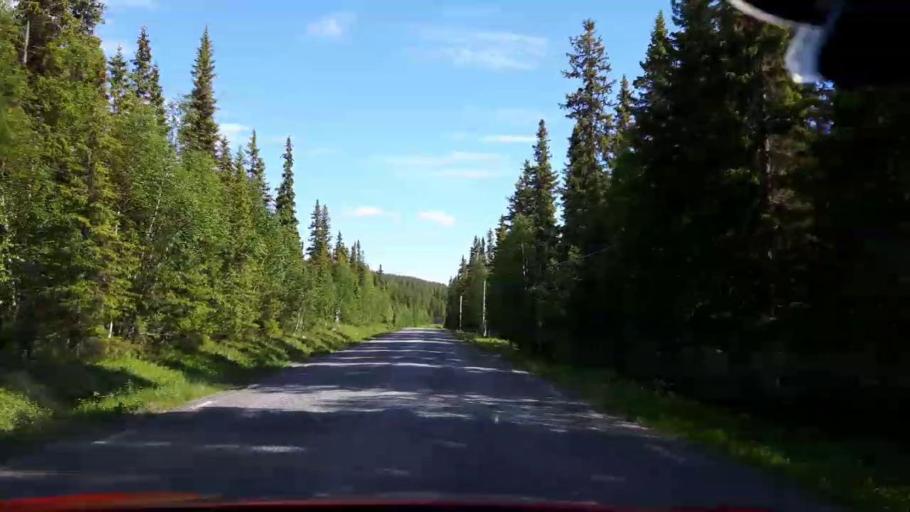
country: SE
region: Jaemtland
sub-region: Krokoms Kommun
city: Valla
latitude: 63.7541
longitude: 14.1117
